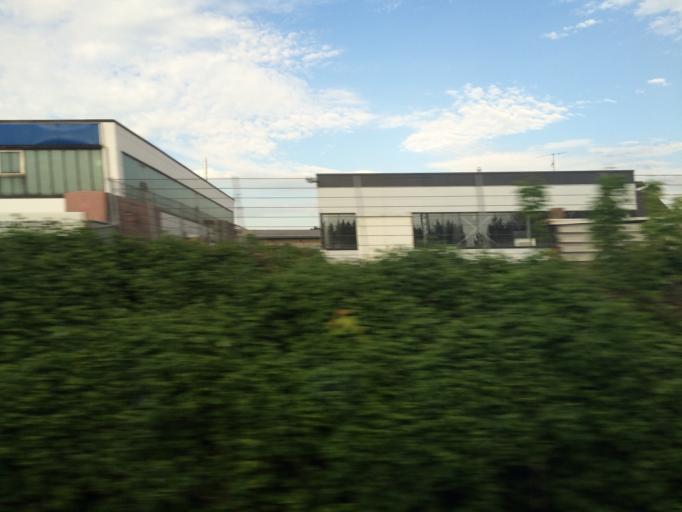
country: DE
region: North Rhine-Westphalia
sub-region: Regierungsbezirk Dusseldorf
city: Langenfeld
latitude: 51.0915
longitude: 6.9451
